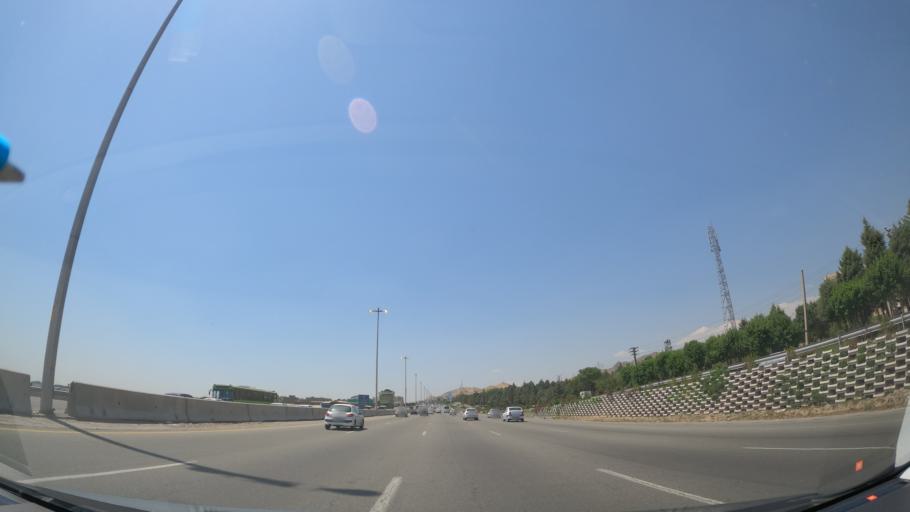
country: IR
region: Alborz
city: Karaj
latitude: 35.7762
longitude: 51.0383
